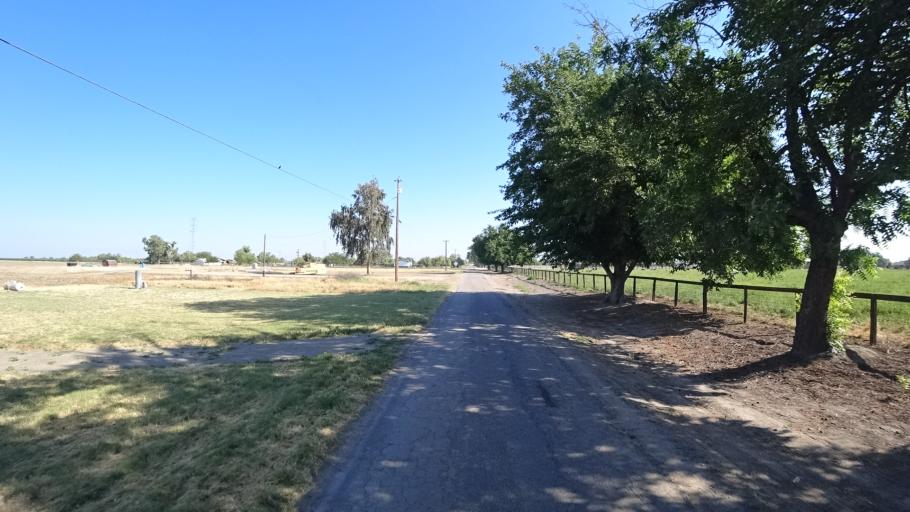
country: US
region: California
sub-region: Fresno County
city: Riverdale
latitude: 36.3777
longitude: -119.8873
